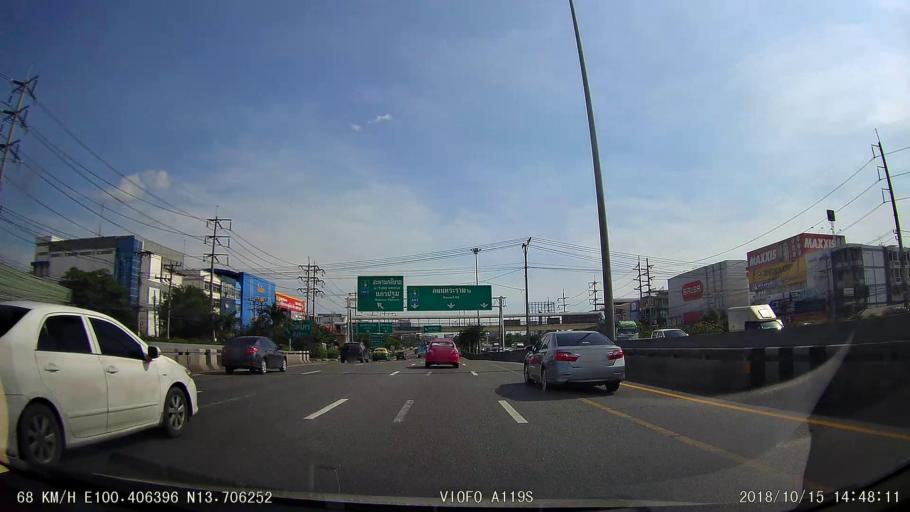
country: TH
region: Bangkok
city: Bang Khae
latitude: 13.7060
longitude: 100.4064
